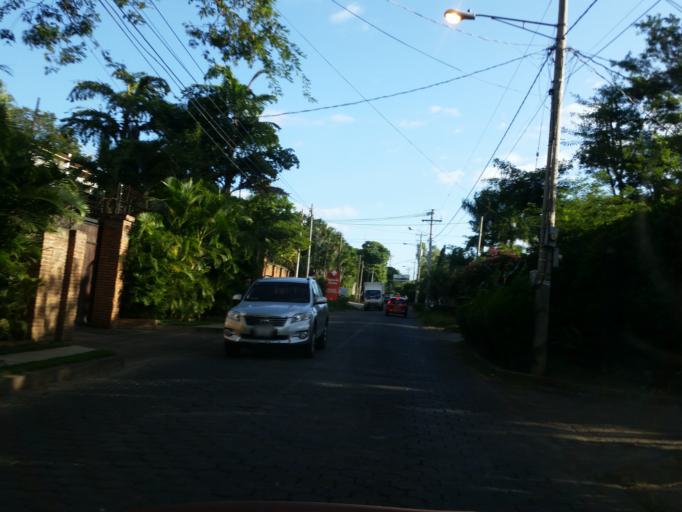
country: NI
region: Managua
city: Managua
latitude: 12.0950
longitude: -86.2349
